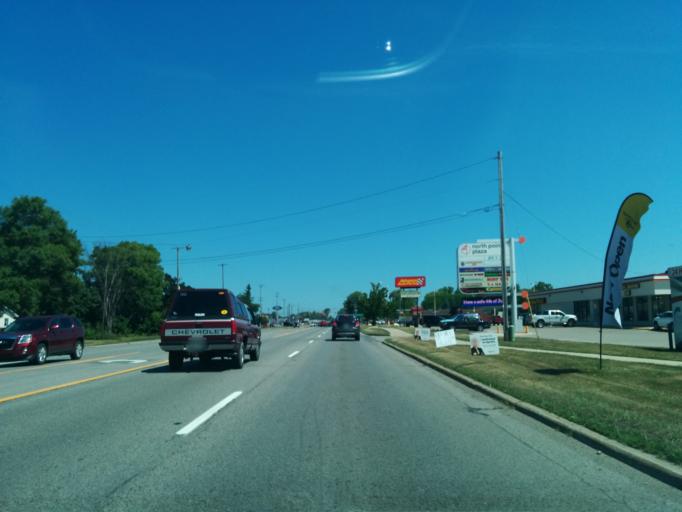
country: US
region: Michigan
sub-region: Bay County
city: Bay City
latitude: 43.6210
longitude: -83.9143
